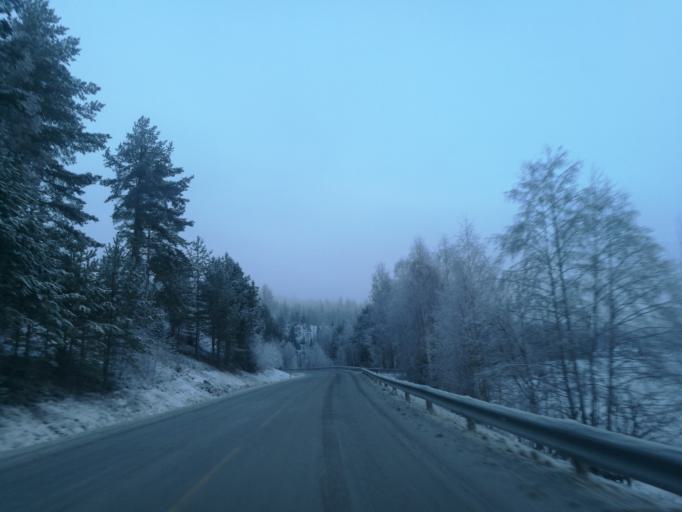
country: NO
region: Hedmark
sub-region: Kongsvinger
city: Kongsvinger
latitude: 60.2797
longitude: 12.1515
